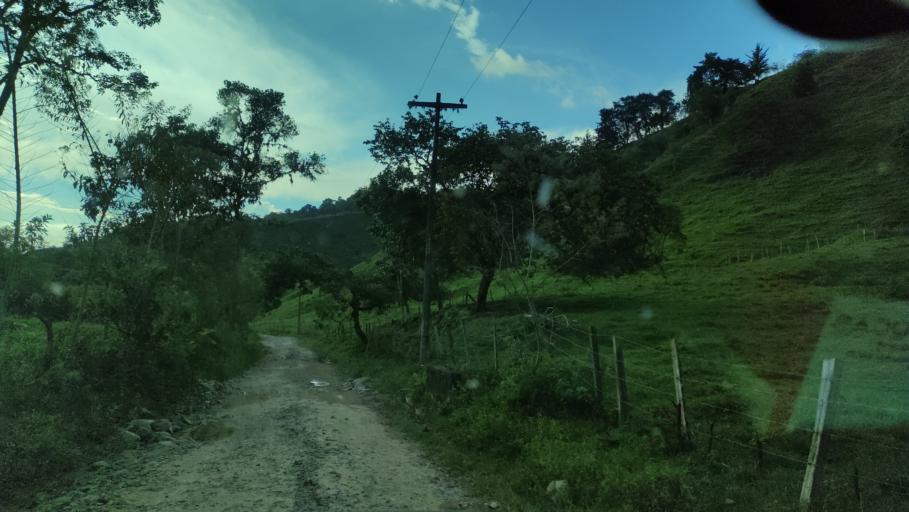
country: CO
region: Valle del Cauca
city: Buga
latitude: 3.8826
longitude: -76.1816
